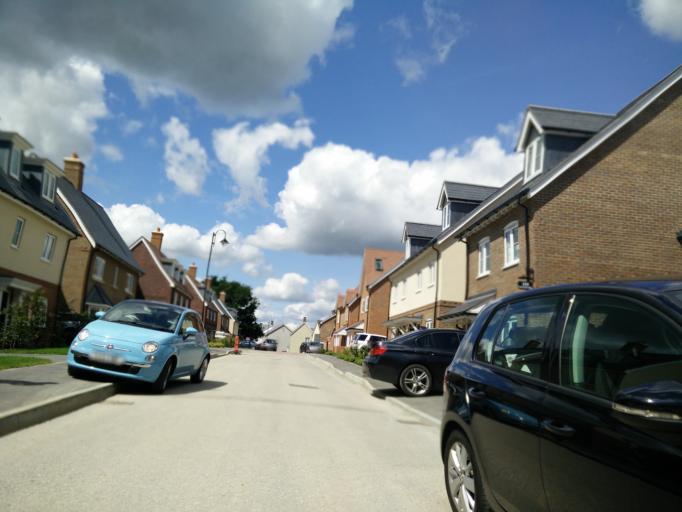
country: GB
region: England
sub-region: West Sussex
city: Horsham
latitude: 51.0623
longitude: -0.3657
